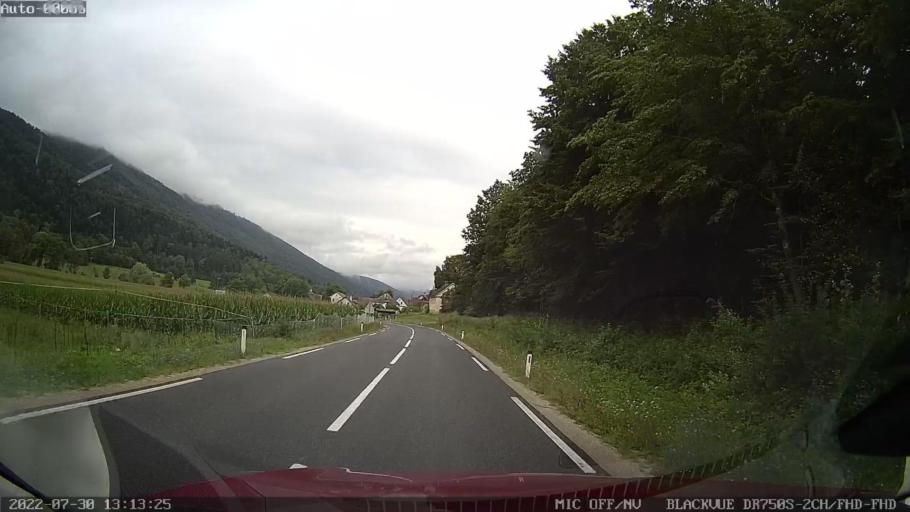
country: SI
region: Dolenjske Toplice
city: Dolenjske Toplice
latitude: 45.7209
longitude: 15.0581
